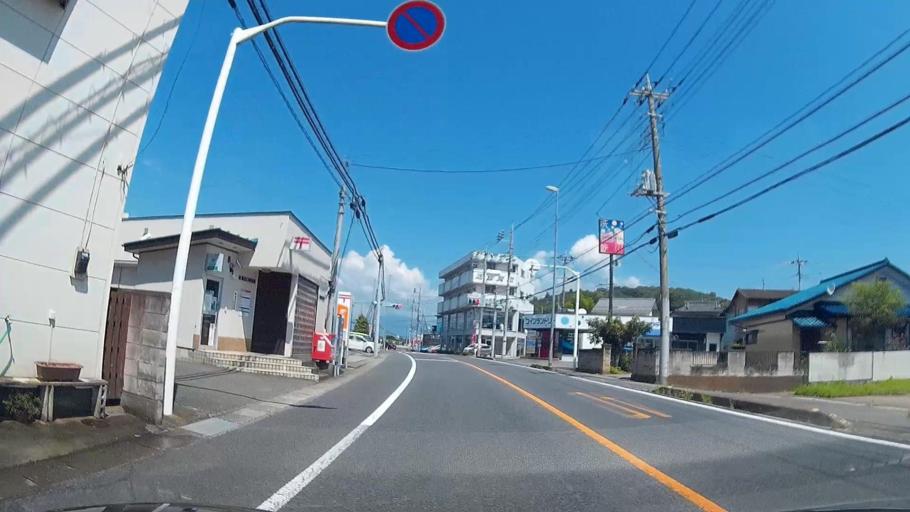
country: JP
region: Gunma
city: Maebashi-shi
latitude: 36.4476
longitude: 139.0469
